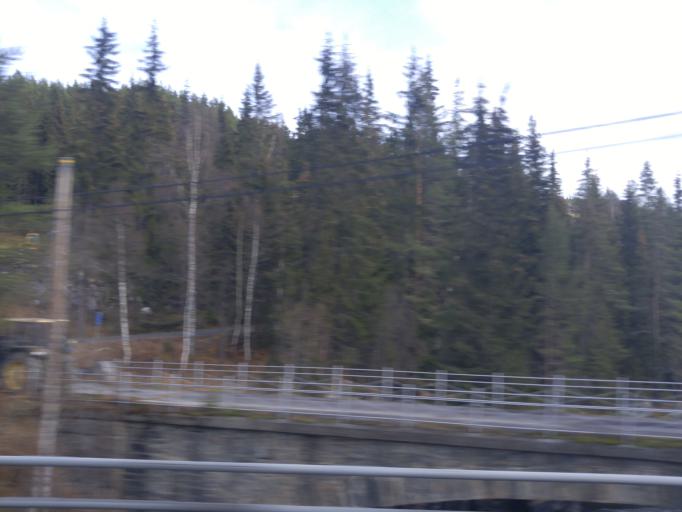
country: NO
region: Oppland
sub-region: Nord-Aurdal
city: Fagernes
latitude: 61.0350
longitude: 9.1771
